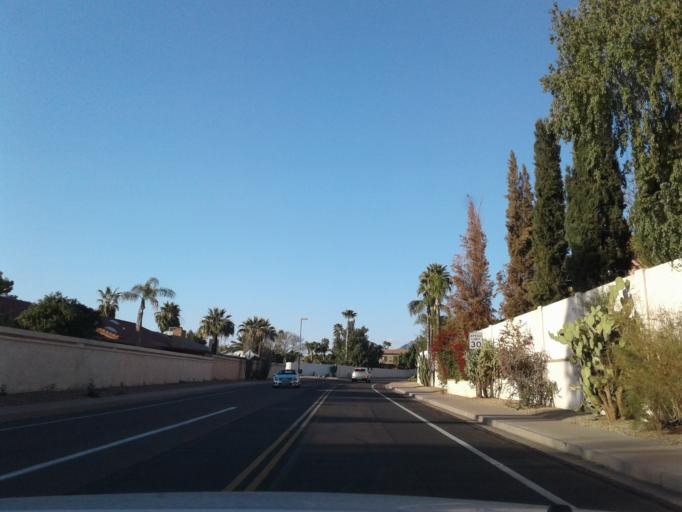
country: US
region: Arizona
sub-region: Maricopa County
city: Scottsdale
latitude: 33.5888
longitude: -111.8437
